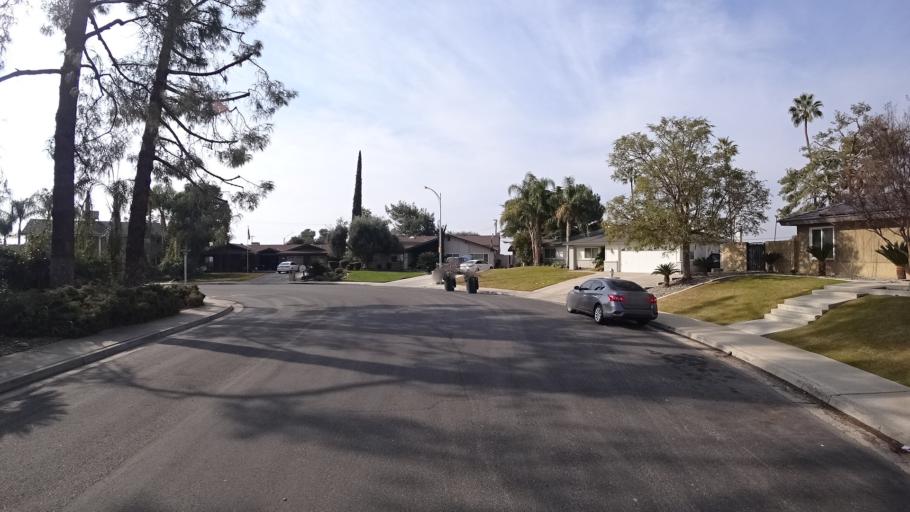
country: US
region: California
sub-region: Kern County
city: Oildale
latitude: 35.4134
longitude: -118.9666
